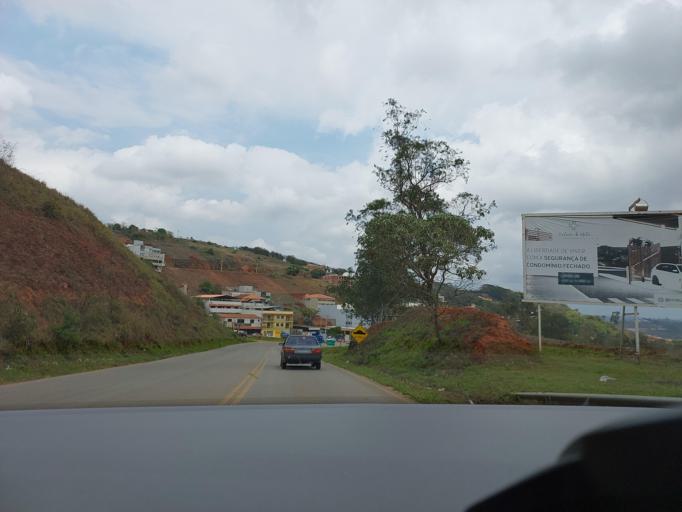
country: BR
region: Minas Gerais
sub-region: Ponte Nova
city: Ponte Nova
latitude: -20.3962
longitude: -42.8774
